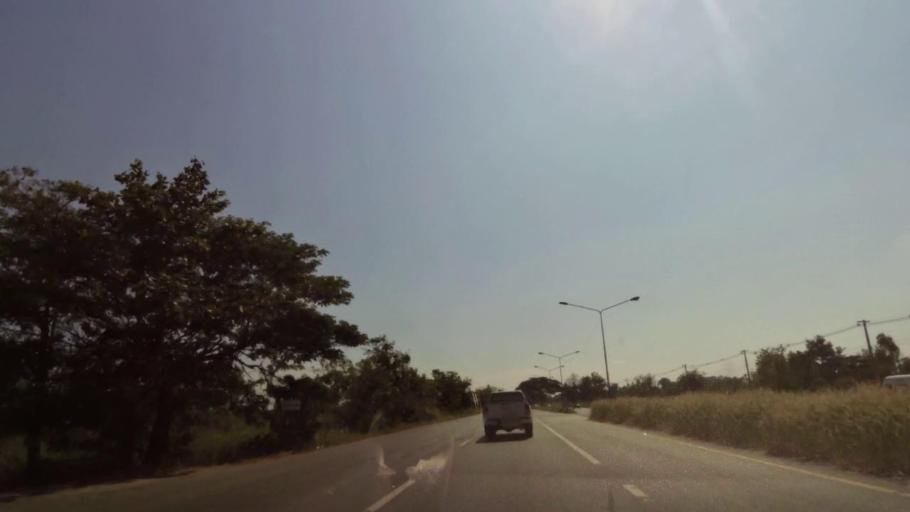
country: TH
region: Nakhon Sawan
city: Kao Liao
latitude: 15.8638
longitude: 100.1167
